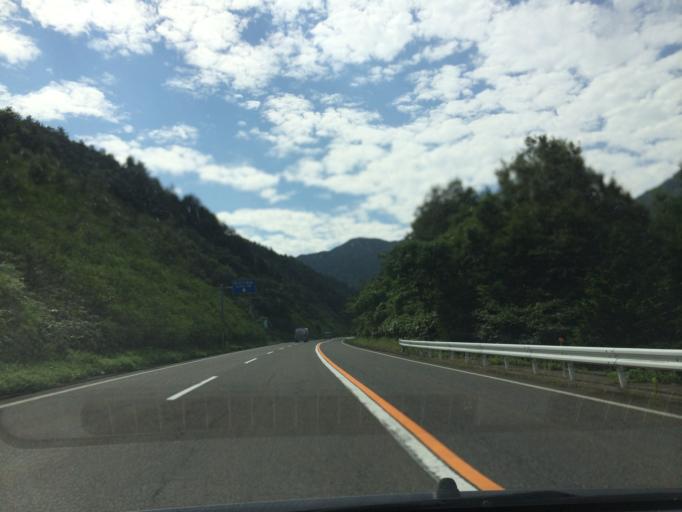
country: JP
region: Tottori
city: Kurayoshi
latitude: 35.3260
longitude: 133.7560
